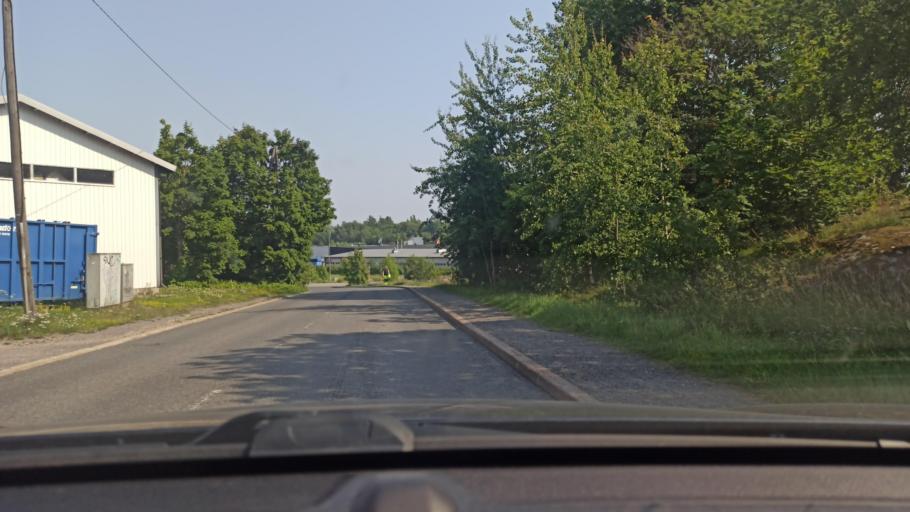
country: FI
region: Varsinais-Suomi
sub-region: Turku
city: Turku
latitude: 60.4596
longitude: 22.2332
